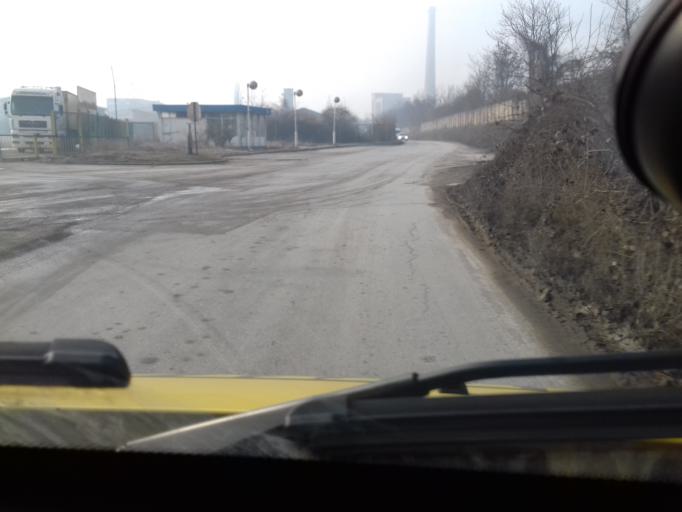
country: BA
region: Federation of Bosnia and Herzegovina
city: Zenica
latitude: 44.2164
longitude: 17.9084
